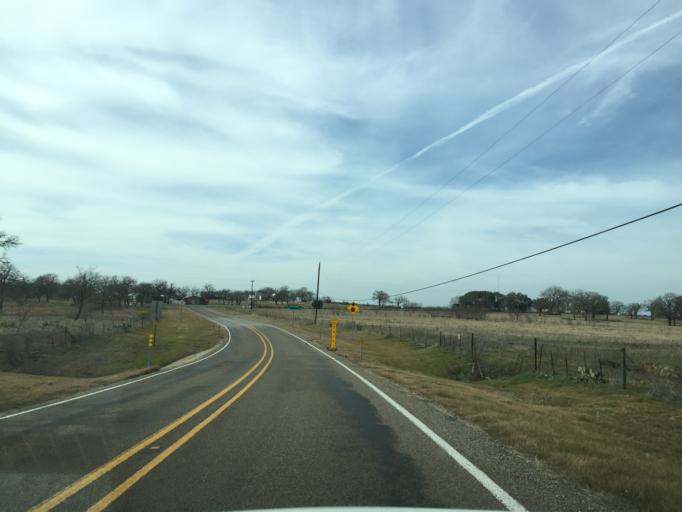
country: US
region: Texas
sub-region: Gillespie County
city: Fredericksburg
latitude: 30.4128
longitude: -98.7337
